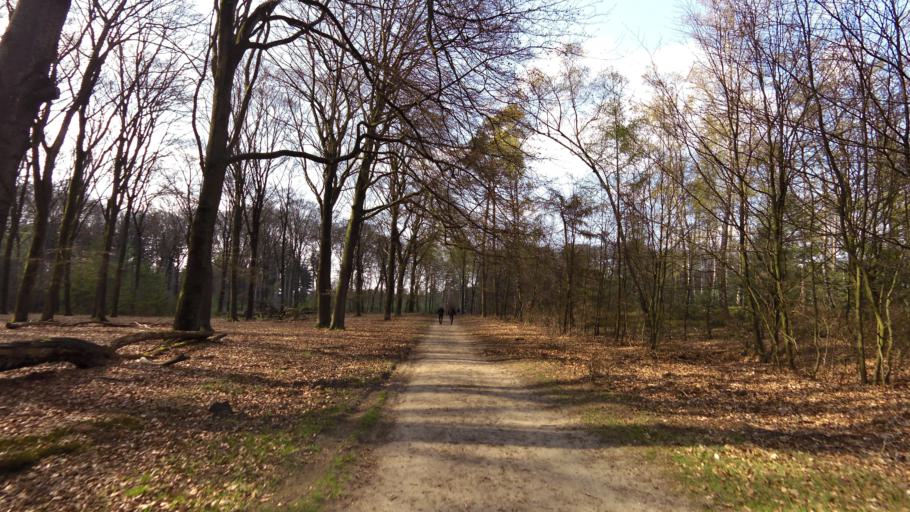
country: NL
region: Gelderland
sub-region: Gemeente Renkum
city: Wolfheze
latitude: 52.0300
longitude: 5.7954
